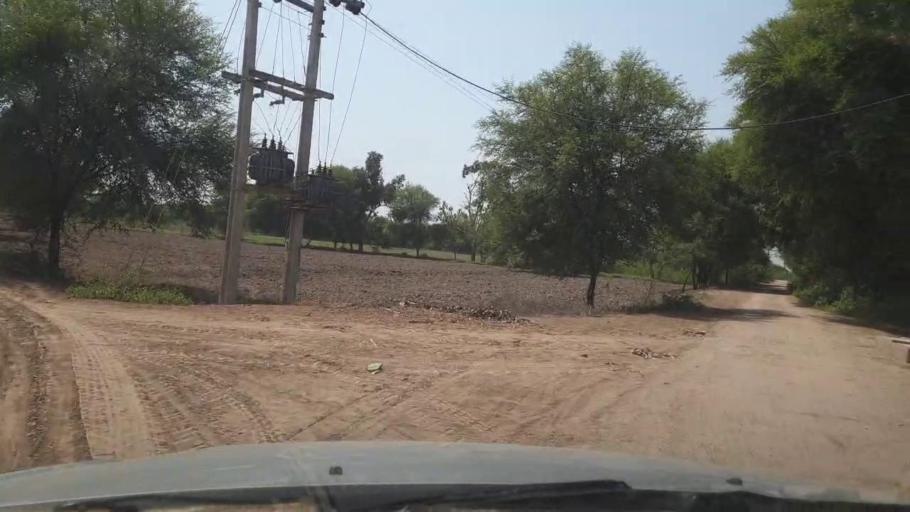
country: PK
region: Sindh
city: Chambar
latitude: 25.2070
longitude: 68.7834
